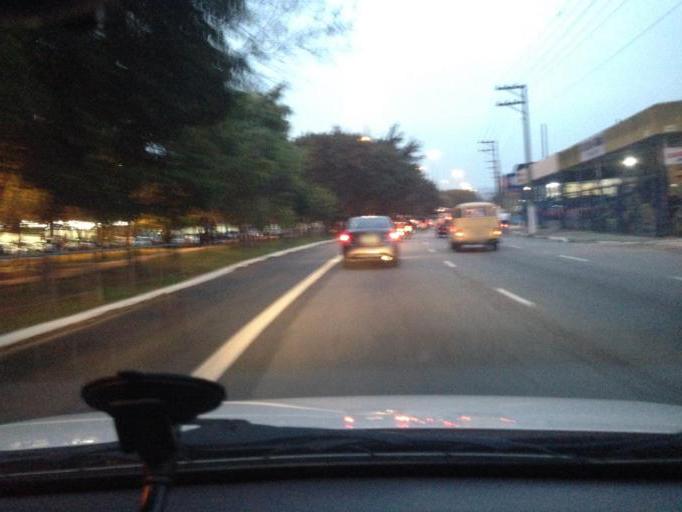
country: BR
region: Sao Paulo
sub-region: Sao Paulo
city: Sao Paulo
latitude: -23.4935
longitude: -46.7094
